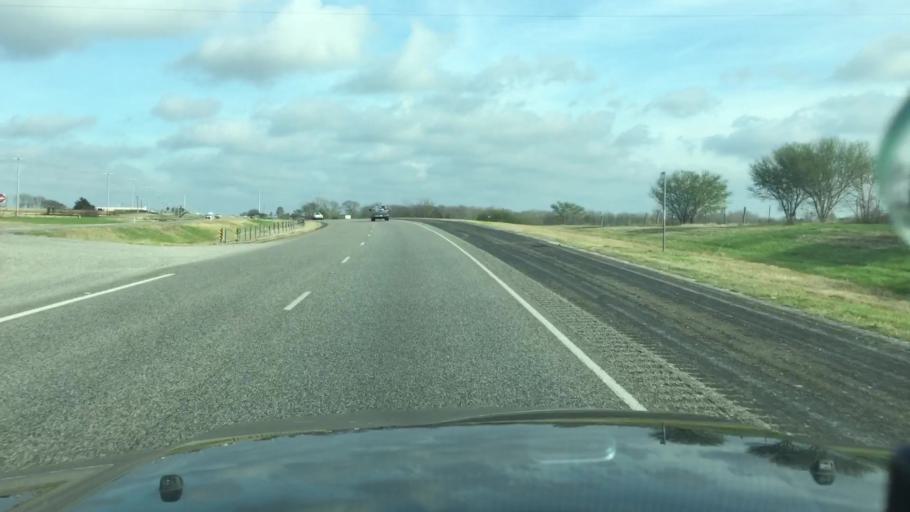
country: US
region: Texas
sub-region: Washington County
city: Brenham
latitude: 30.1363
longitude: -96.3375
